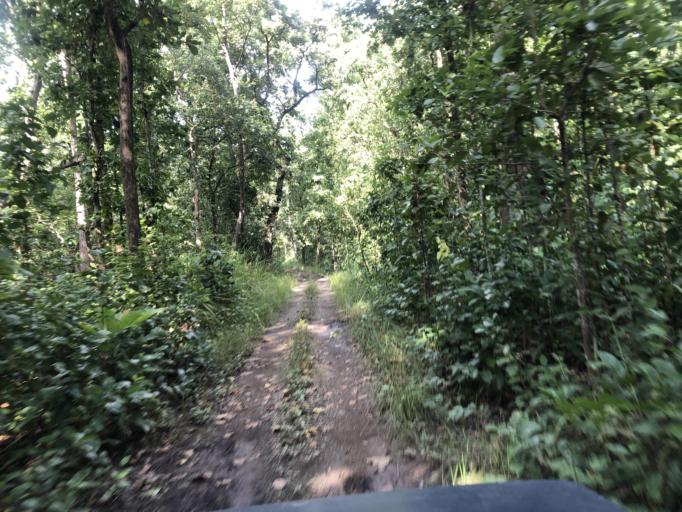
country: NP
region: Far Western
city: Tikapur
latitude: 28.5510
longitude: 81.2897
